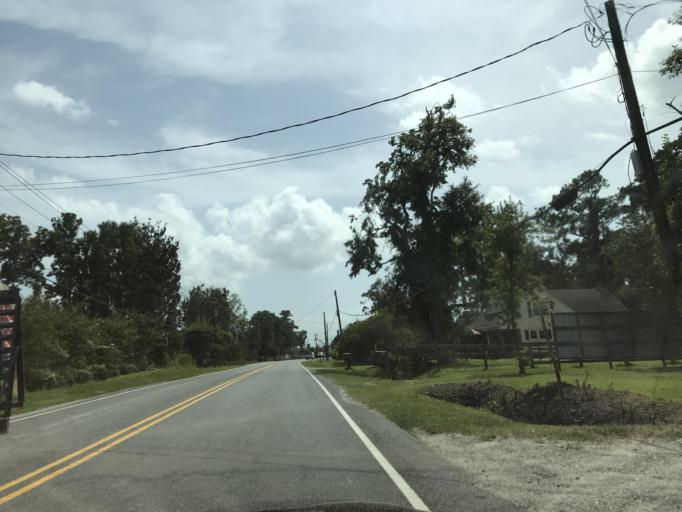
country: US
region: North Carolina
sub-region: New Hanover County
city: Wrightsboro
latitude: 34.2713
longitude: -77.9272
